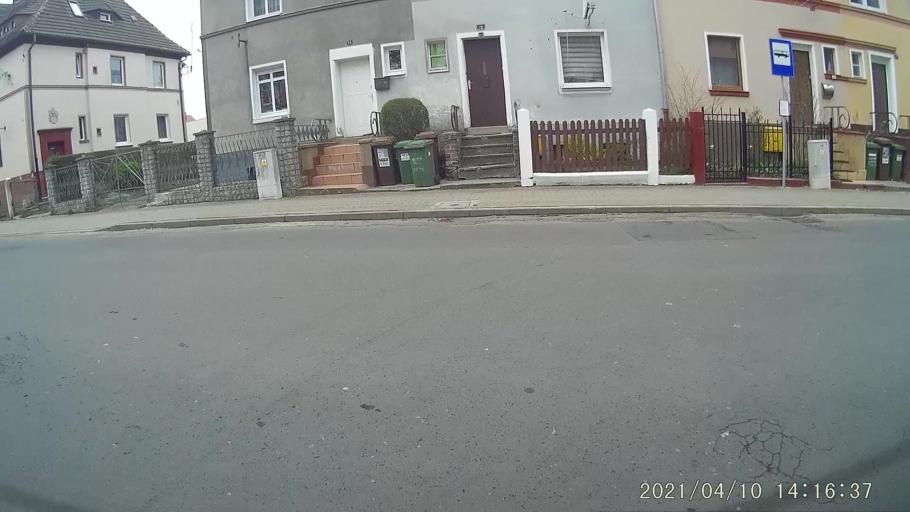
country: PL
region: Lower Silesian Voivodeship
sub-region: Powiat zgorzelecki
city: Lagow
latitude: 51.1592
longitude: 15.0418
